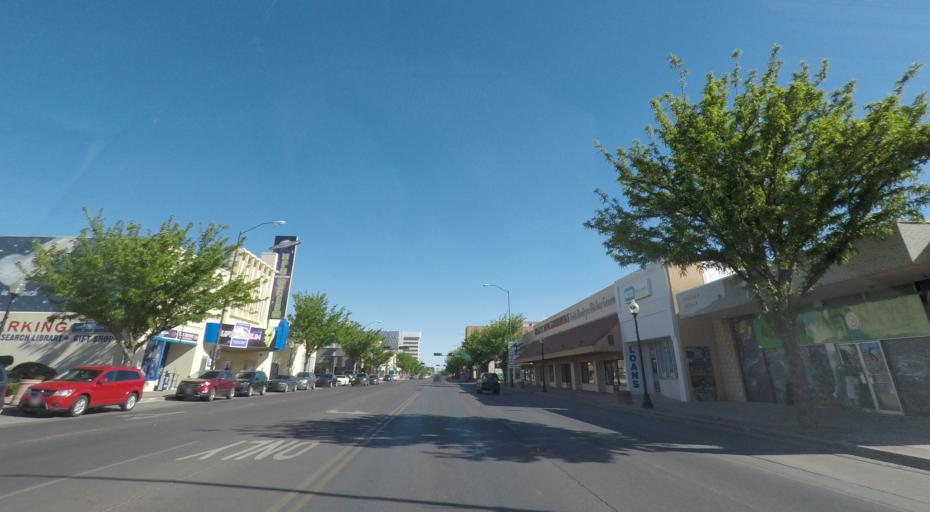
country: US
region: New Mexico
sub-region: Chaves County
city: Roswell
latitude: 33.3932
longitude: -104.5228
